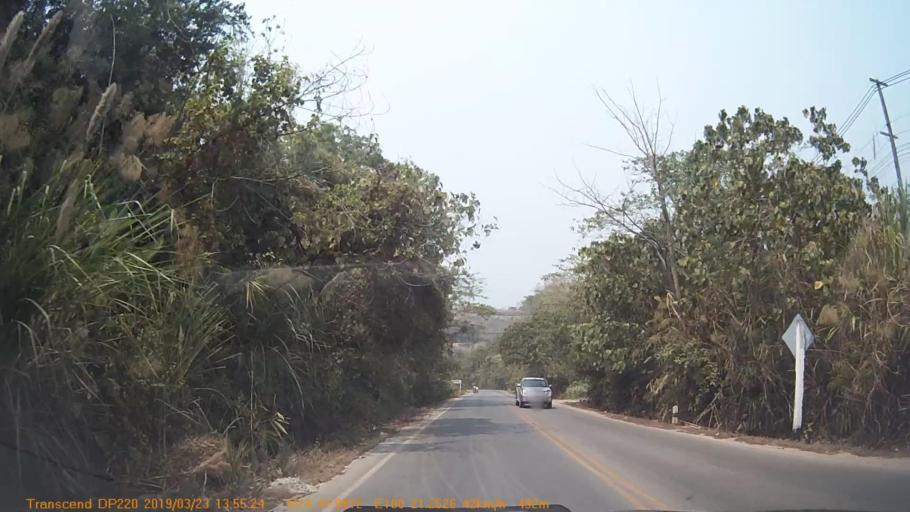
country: TH
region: Chiang Rai
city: Khun Tan
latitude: 19.8000
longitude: 100.3542
